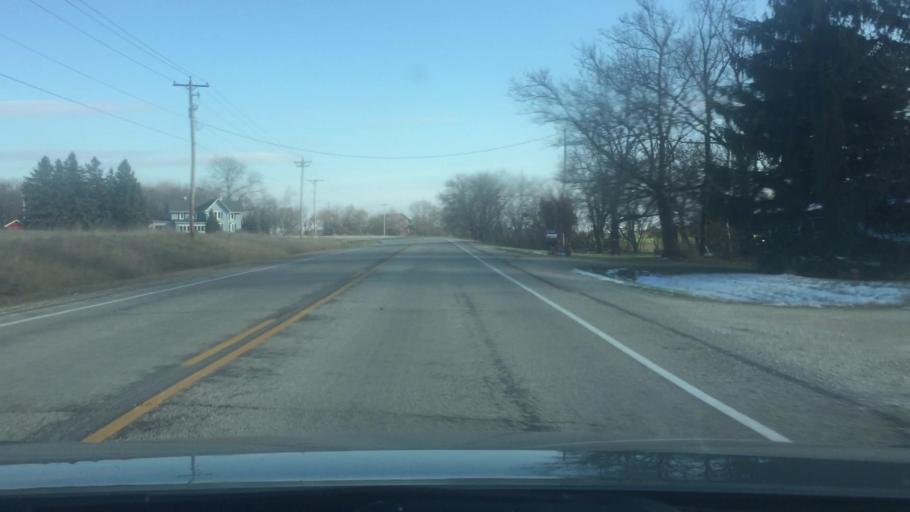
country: US
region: Wisconsin
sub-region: Walworth County
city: Whitewater
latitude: 42.9322
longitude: -88.7232
